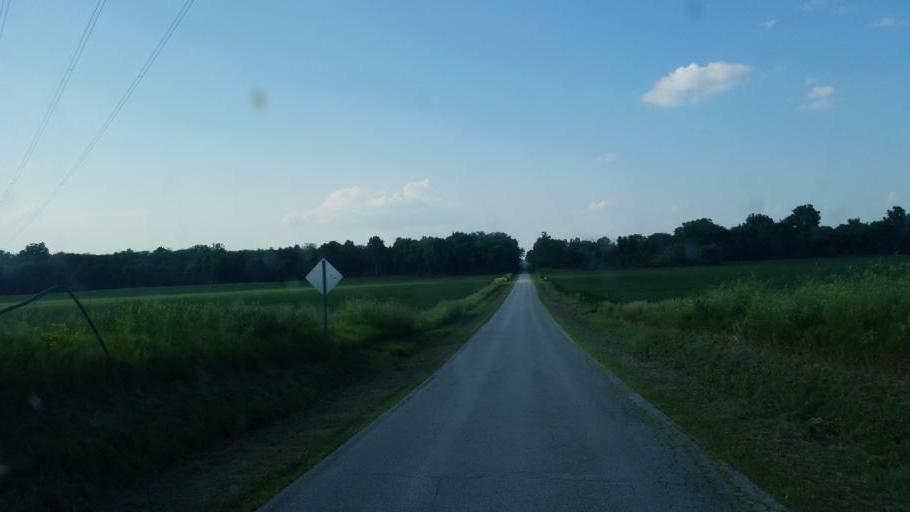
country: US
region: Ohio
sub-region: Crawford County
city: Bucyrus
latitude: 40.8500
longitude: -83.0739
